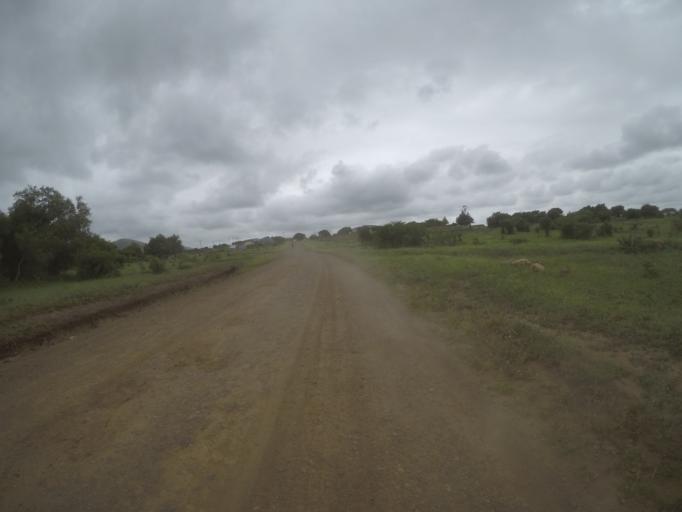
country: ZA
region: KwaZulu-Natal
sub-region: uThungulu District Municipality
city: Empangeni
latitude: -28.6103
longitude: 31.8636
